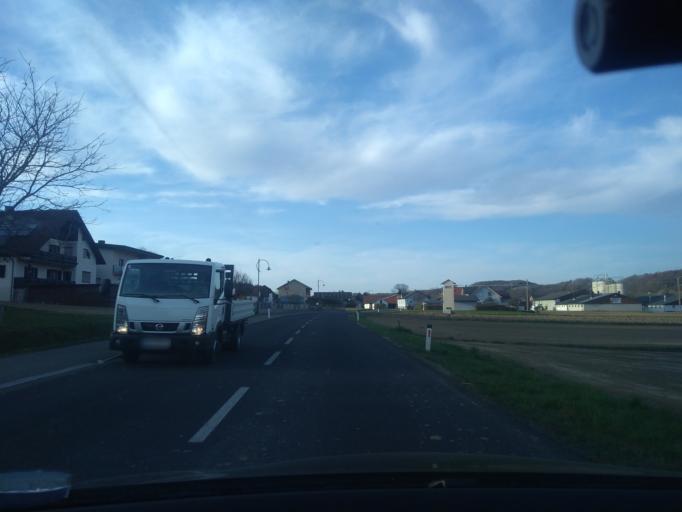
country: AT
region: Styria
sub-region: Politischer Bezirk Suedoststeiermark
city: Jagerberg
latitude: 46.8661
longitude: 15.7252
